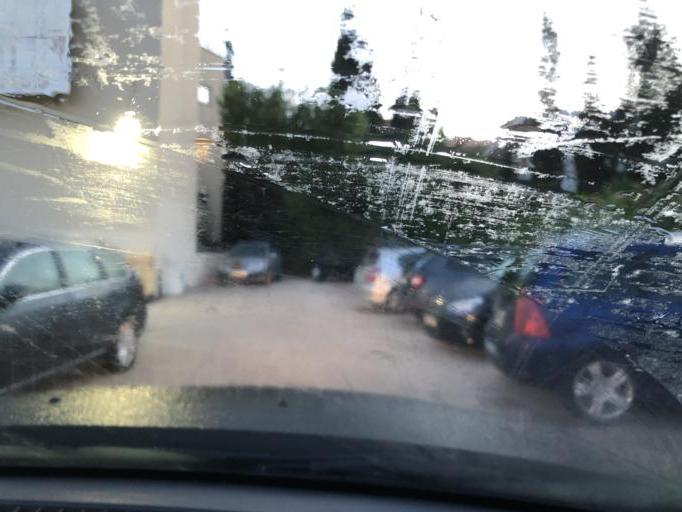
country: ES
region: Balearic Islands
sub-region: Illes Balears
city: Camp de Mar
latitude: 39.5425
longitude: 2.3869
